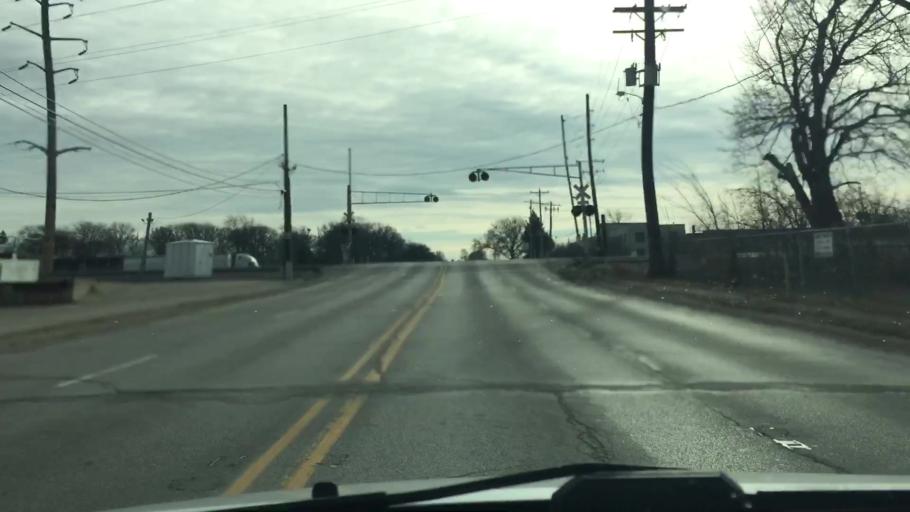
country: US
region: Illinois
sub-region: Kane County
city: Elgin
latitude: 42.0129
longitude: -88.2693
